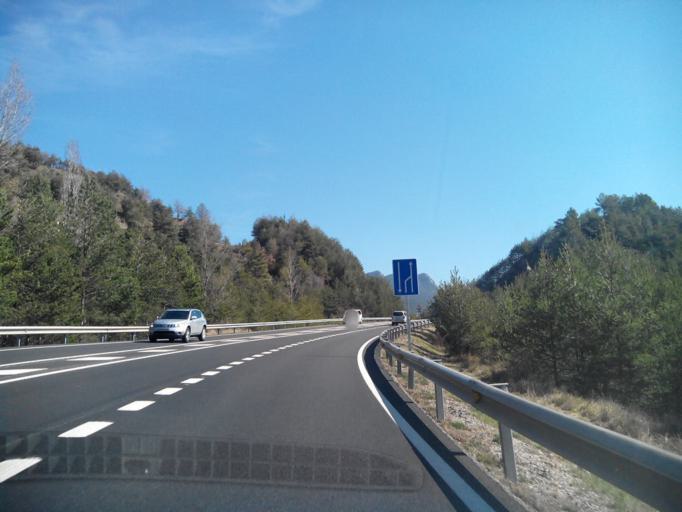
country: ES
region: Catalonia
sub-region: Provincia de Barcelona
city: Berga
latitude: 42.1255
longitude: 1.8579
